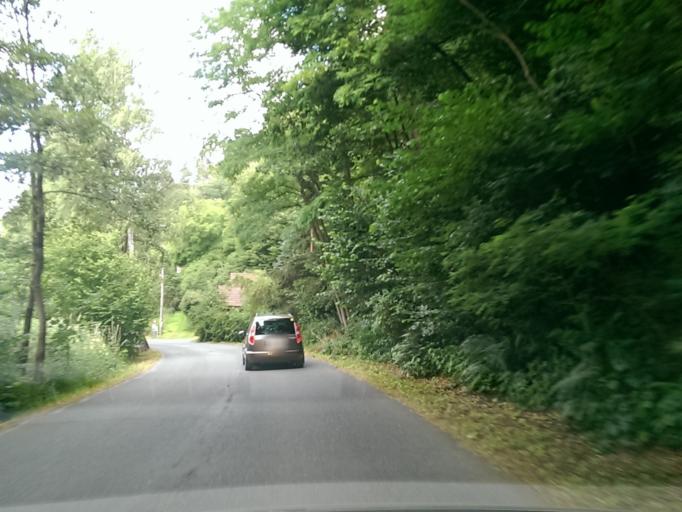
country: CZ
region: Central Bohemia
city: Mseno
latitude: 50.4319
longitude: 14.5823
